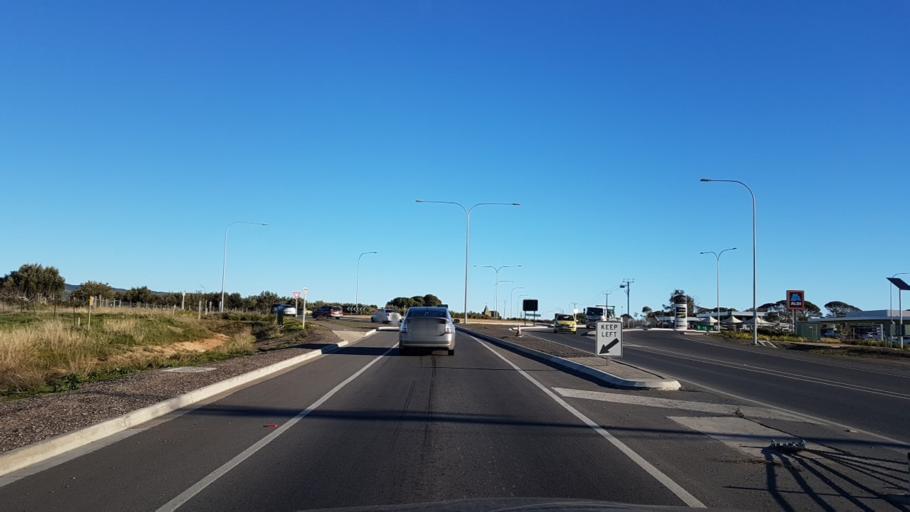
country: AU
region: South Australia
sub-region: Onkaparinga
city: Aldinga
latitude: -35.2669
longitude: 138.4857
